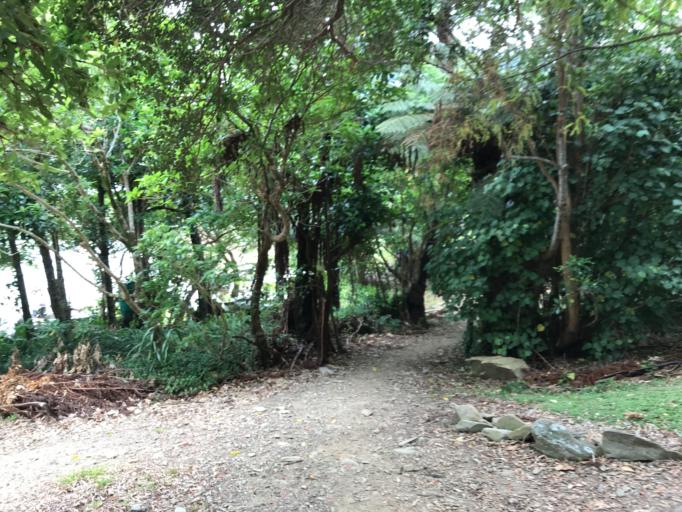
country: NZ
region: Marlborough
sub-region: Marlborough District
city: Picton
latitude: -41.1043
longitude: 174.1841
